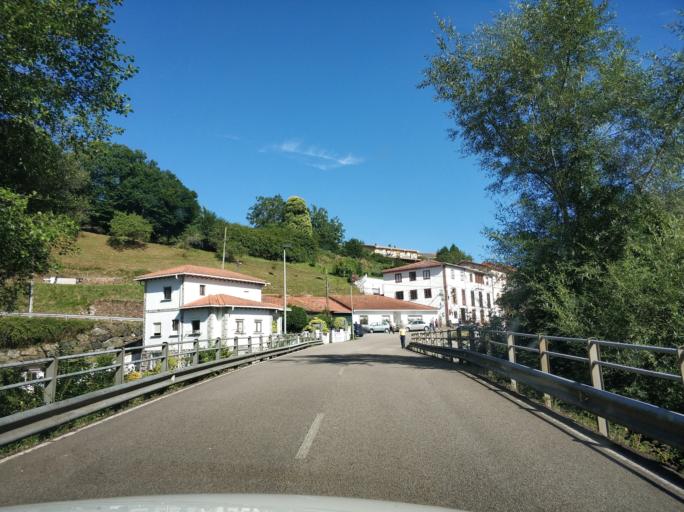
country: ES
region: Asturias
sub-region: Province of Asturias
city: Cudillero
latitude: 43.5597
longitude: -6.2300
